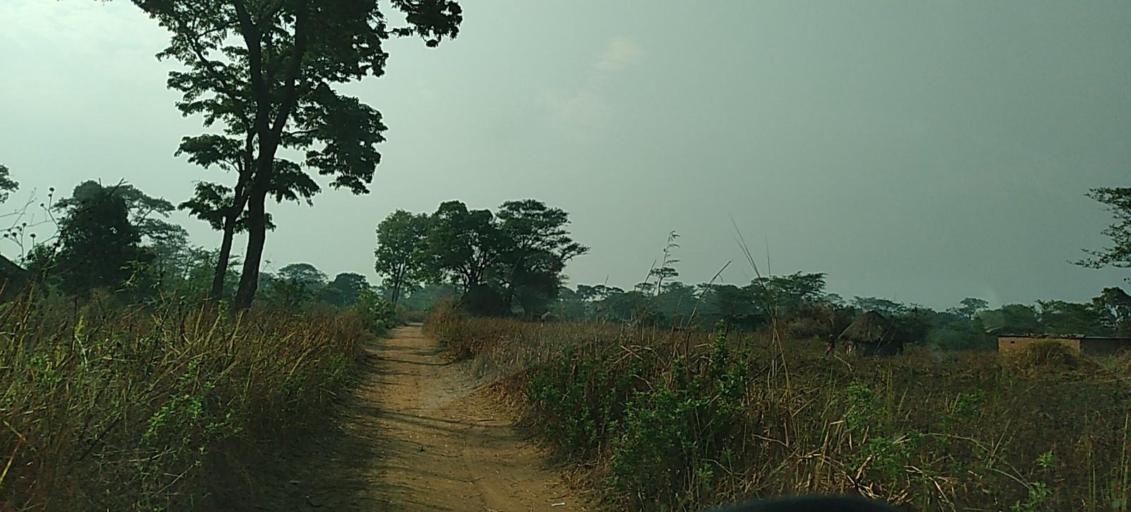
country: ZM
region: North-Western
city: Solwezi
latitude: -12.3679
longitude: 26.5573
